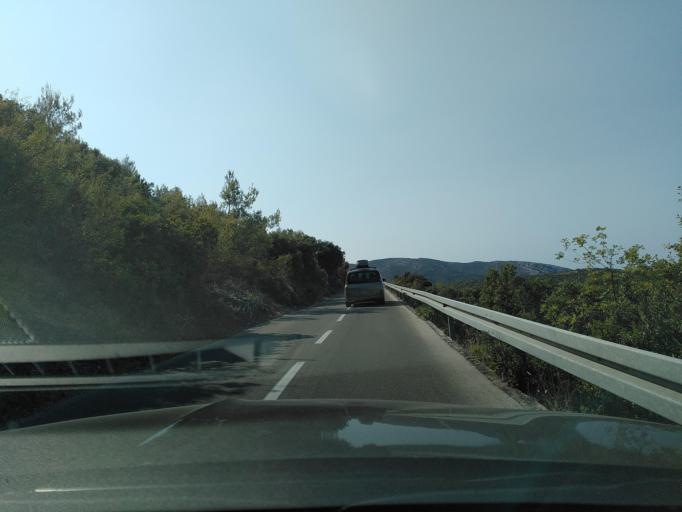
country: HR
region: Splitsko-Dalmatinska
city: Stari Grad
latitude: 43.1650
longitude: 16.5645
